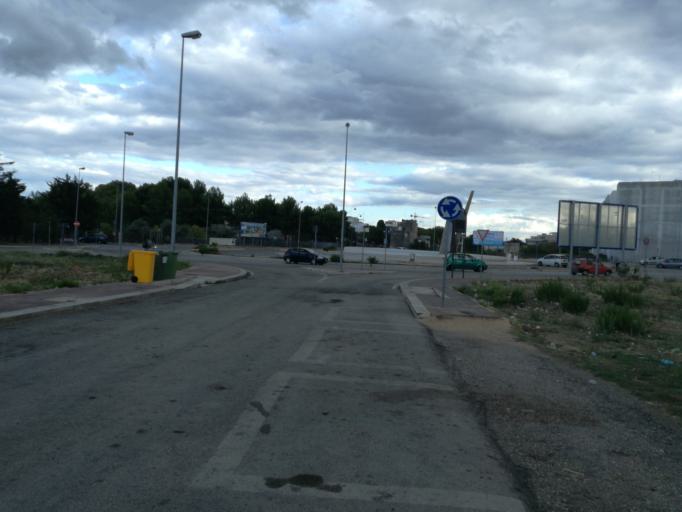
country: IT
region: Apulia
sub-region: Provincia di Bari
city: Triggiano
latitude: 41.0684
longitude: 16.9279
